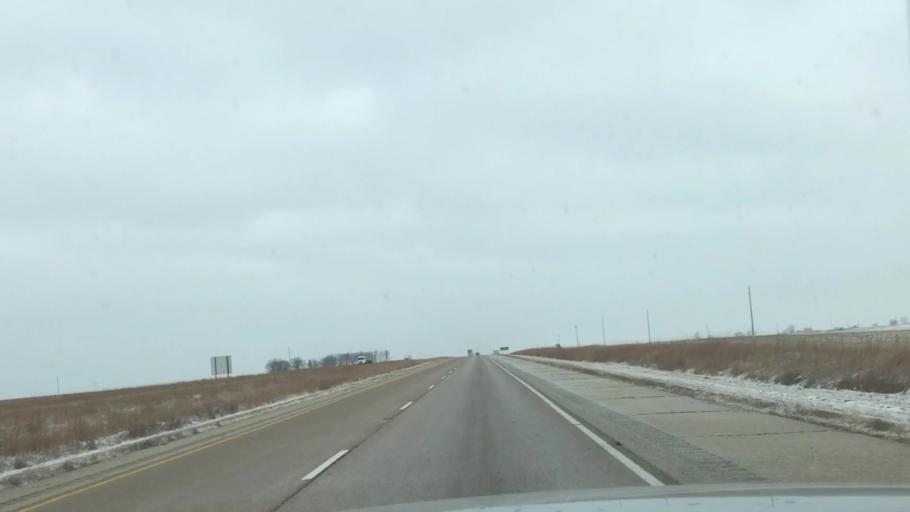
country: US
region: Illinois
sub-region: Montgomery County
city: Raymond
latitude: 39.2971
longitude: -89.6419
